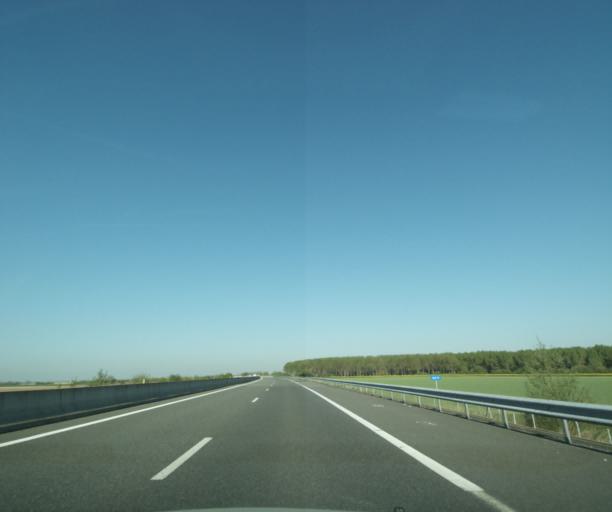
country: FR
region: Centre
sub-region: Departement du Loiret
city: Corbeilles
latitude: 48.0951
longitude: 2.5754
